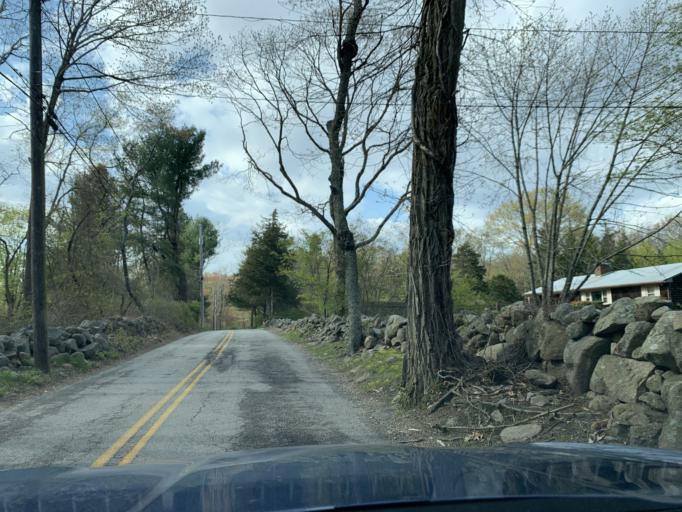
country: US
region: Rhode Island
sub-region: Washington County
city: Exeter
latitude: 41.6030
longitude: -71.5206
